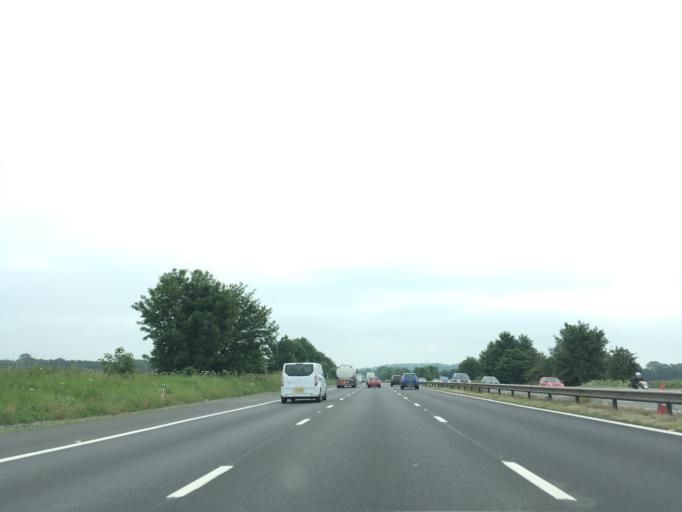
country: GB
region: England
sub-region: West Berkshire
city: Wickham
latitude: 51.4486
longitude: -1.4617
